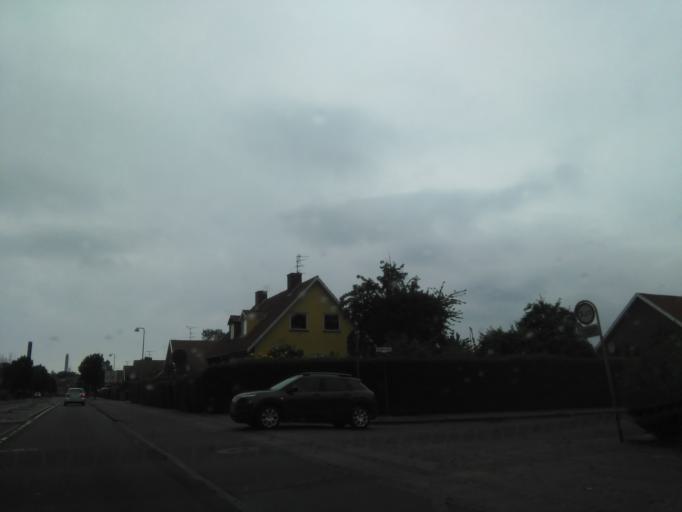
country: DK
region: Capital Region
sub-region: Bornholm Kommune
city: Ronne
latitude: 55.0956
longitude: 14.7080
